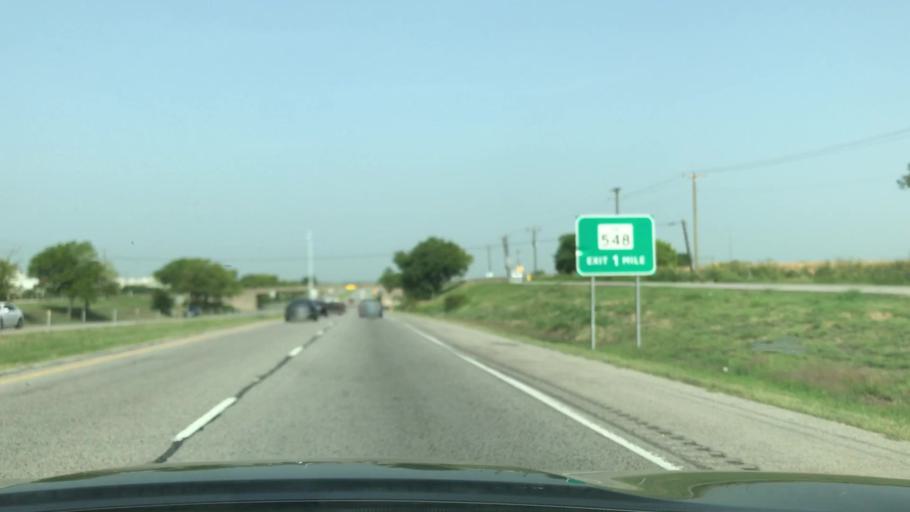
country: US
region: Texas
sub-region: Kaufman County
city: Forney
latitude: 32.7410
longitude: -96.4271
